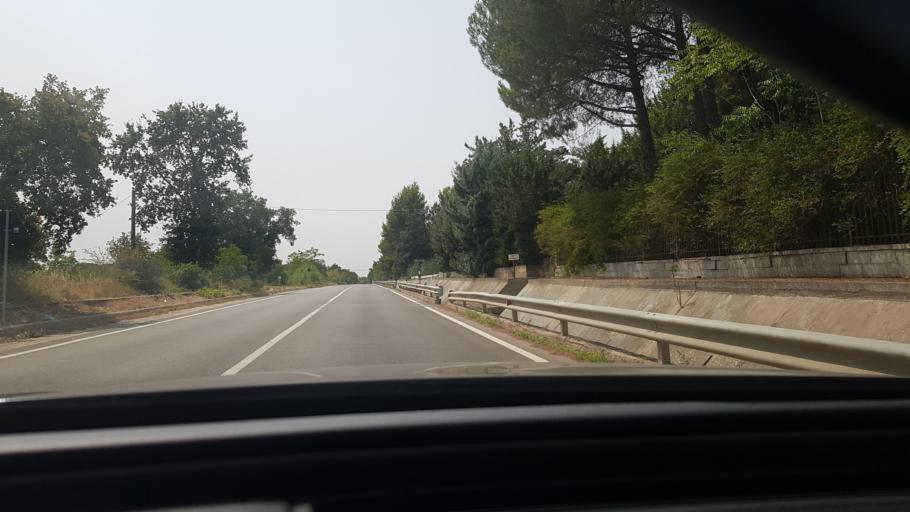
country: IT
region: Apulia
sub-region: Provincia di Barletta - Andria - Trani
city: Andria
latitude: 41.2130
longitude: 16.2717
